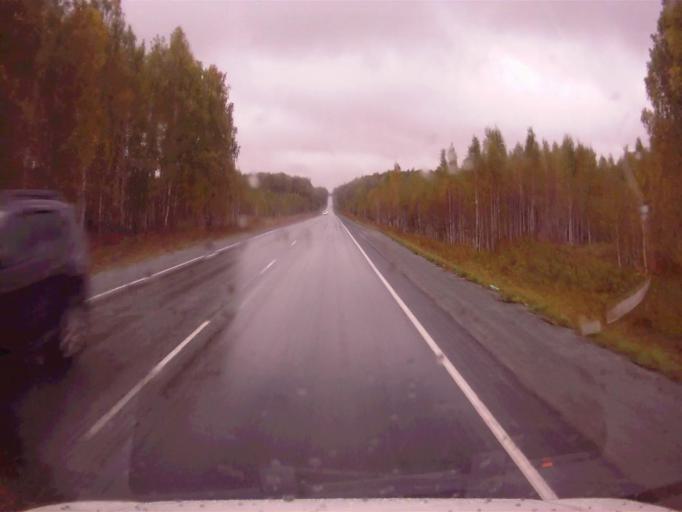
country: RU
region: Chelyabinsk
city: Tayginka
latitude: 55.5141
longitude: 60.6397
